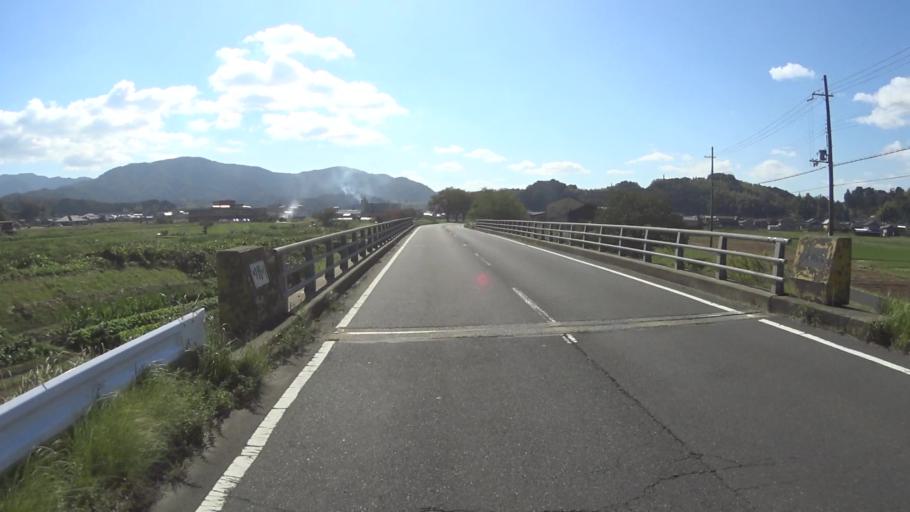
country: JP
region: Kyoto
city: Miyazu
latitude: 35.6646
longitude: 135.0859
